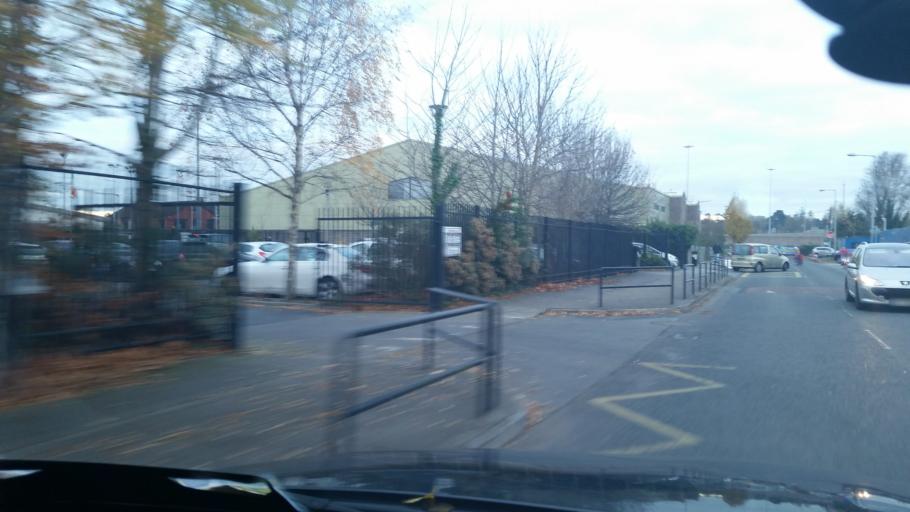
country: IE
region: Leinster
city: Castleknock
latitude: 53.3798
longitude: -6.3617
